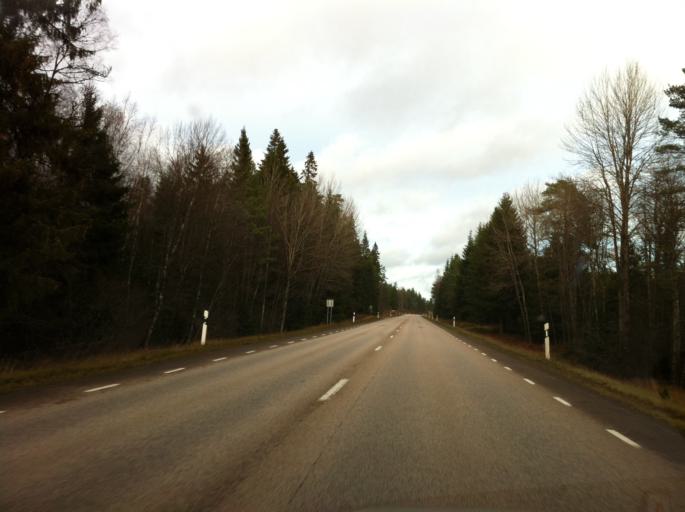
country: SE
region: Kronoberg
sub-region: Uppvidinge Kommun
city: Lenhovda
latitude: 57.1155
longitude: 15.2181
